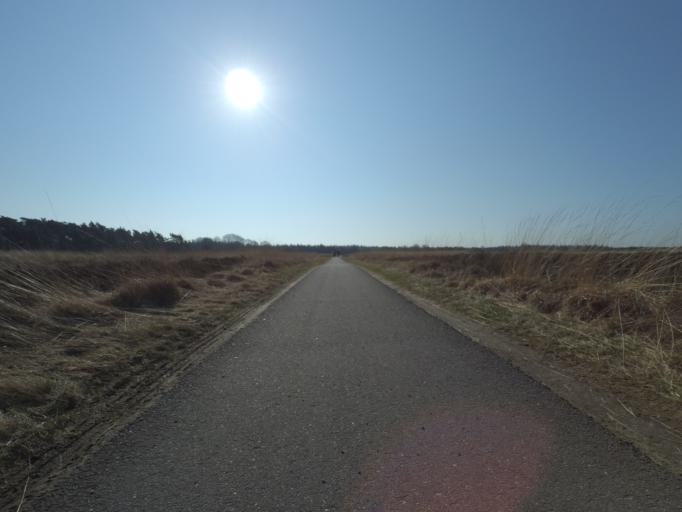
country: NL
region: Gelderland
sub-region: Gemeente Renkum
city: Wolfheze
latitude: 52.0451
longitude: 5.8300
